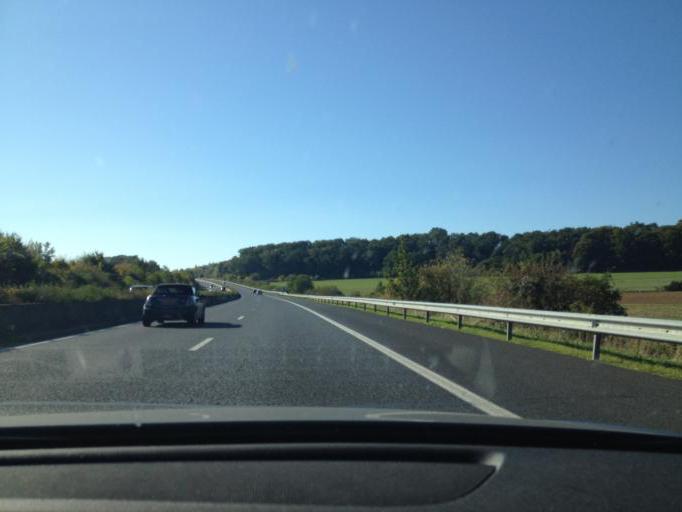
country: LU
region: Grevenmacher
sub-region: Canton de Remich
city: Mondorf-les-Bains
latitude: 49.5196
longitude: 6.2668
